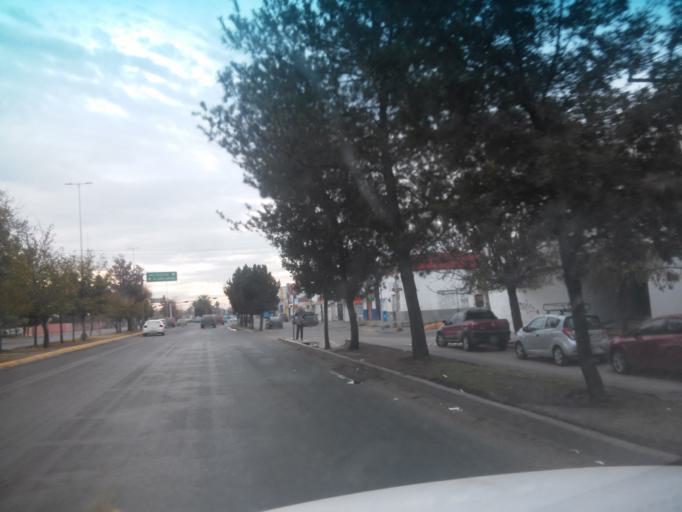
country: MX
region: Durango
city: Victoria de Durango
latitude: 24.0056
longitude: -104.6564
